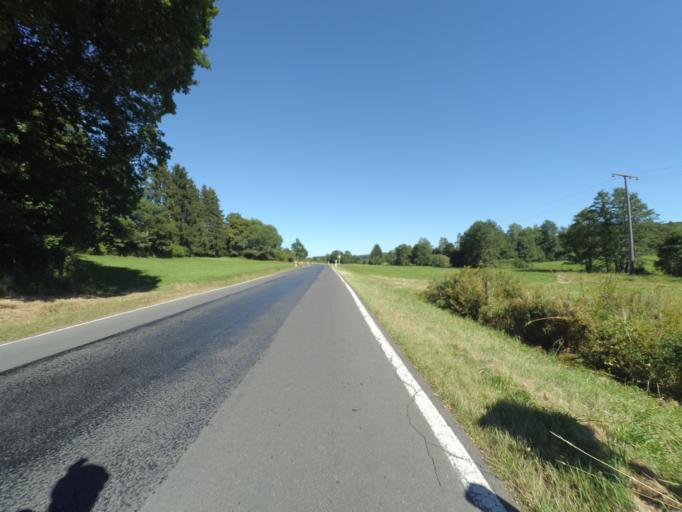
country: DE
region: Rheinland-Pfalz
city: Bongard
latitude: 50.2882
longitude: 6.8464
